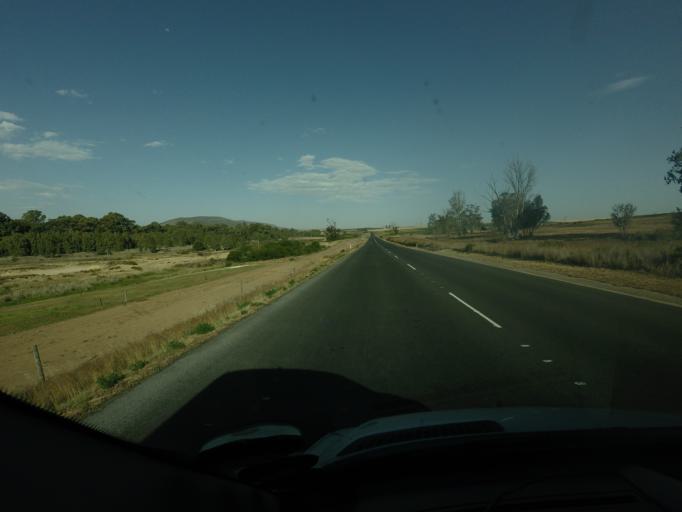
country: ZA
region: Western Cape
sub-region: Cape Winelands District Municipality
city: Ashton
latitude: -34.0869
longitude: 20.1025
